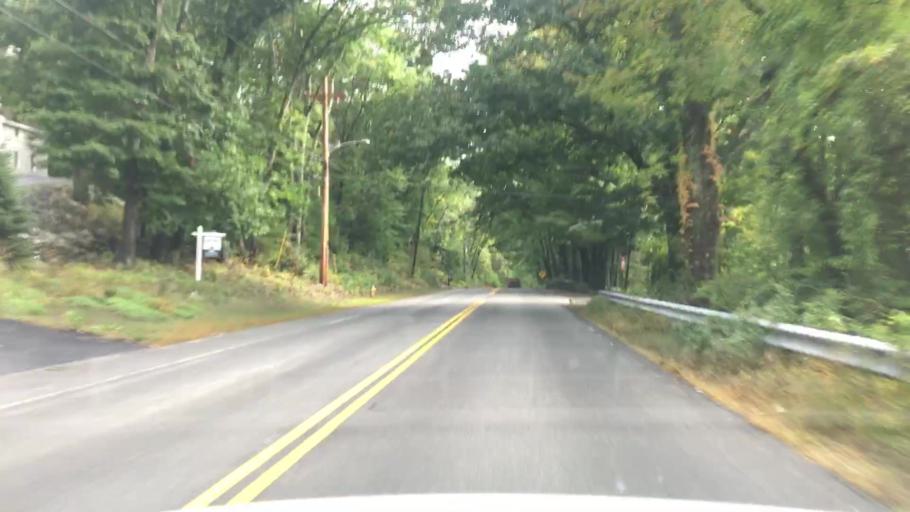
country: US
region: Maine
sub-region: Cumberland County
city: Yarmouth
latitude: 43.7737
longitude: -70.1899
